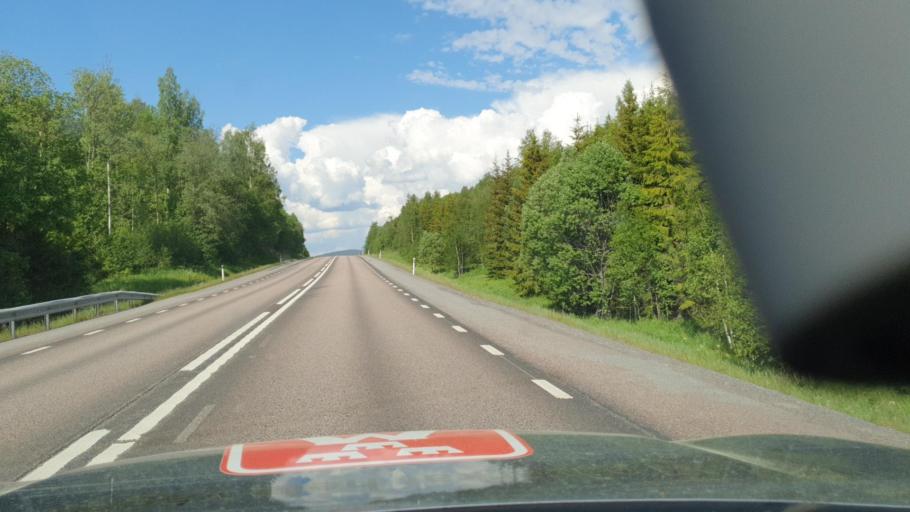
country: SE
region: Vaesternorrland
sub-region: Haernoesands Kommun
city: Haernoesand
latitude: 62.7939
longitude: 17.8966
